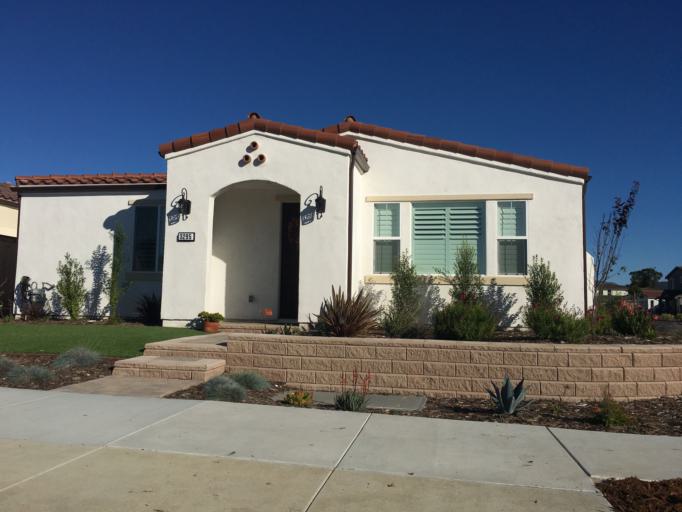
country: US
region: California
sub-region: San Luis Obispo County
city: San Luis Obispo
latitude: 35.2549
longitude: -120.6601
